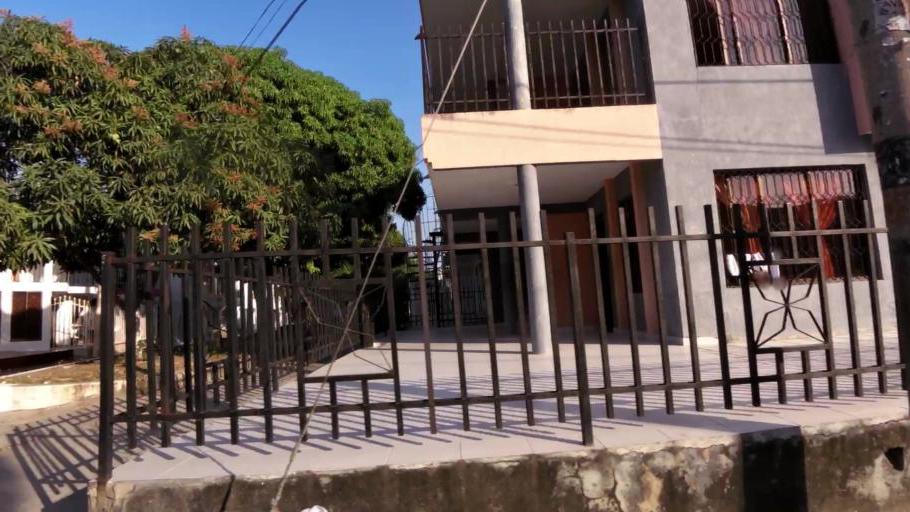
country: CO
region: Bolivar
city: Cartagena
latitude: 10.3819
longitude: -75.4796
